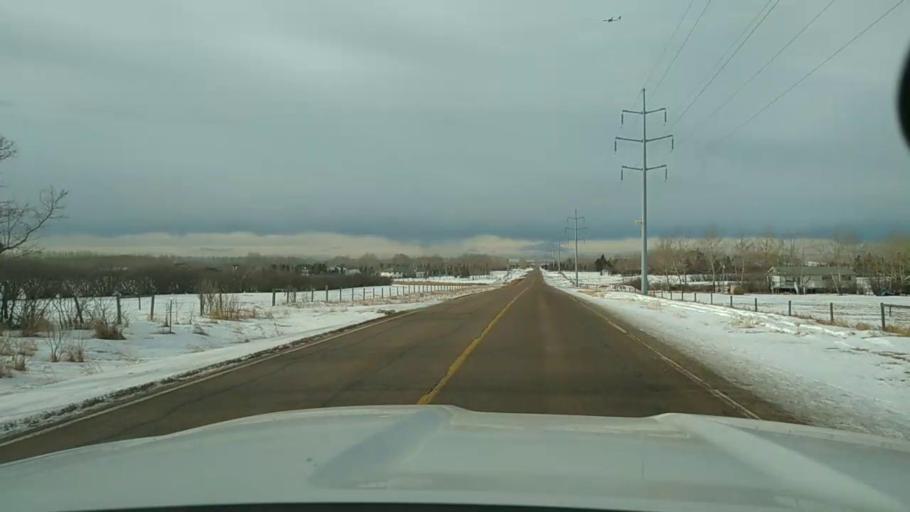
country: CA
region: Alberta
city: Airdrie
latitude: 51.2417
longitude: -113.9653
